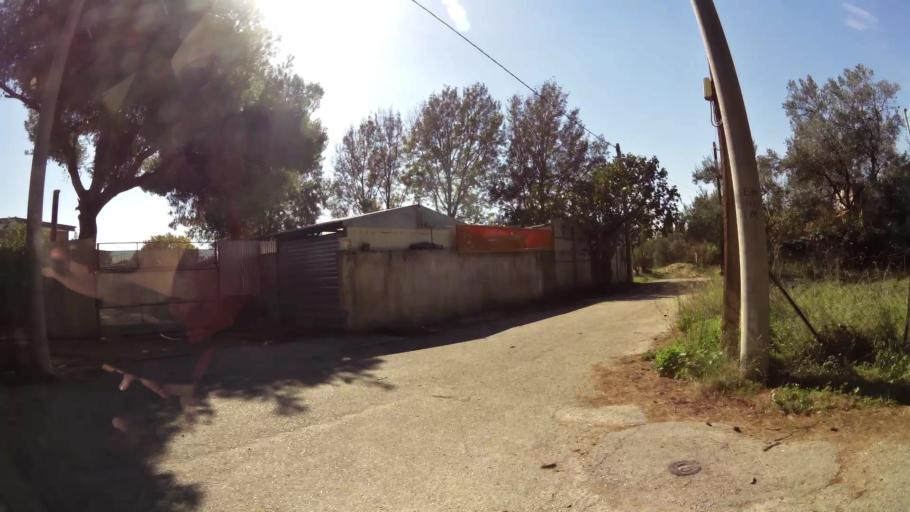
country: GR
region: Attica
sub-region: Nomarchia Athinas
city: Lykovrysi
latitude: 38.0831
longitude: 23.7767
